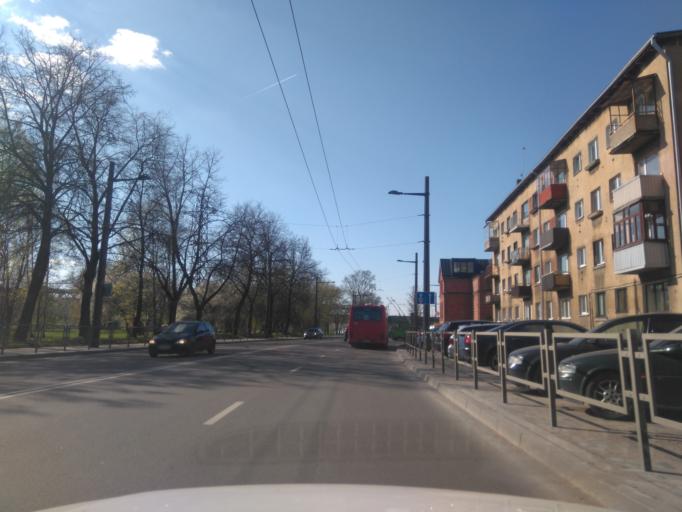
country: LT
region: Kauno apskritis
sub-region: Kaunas
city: Aleksotas
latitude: 54.8806
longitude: 23.9298
